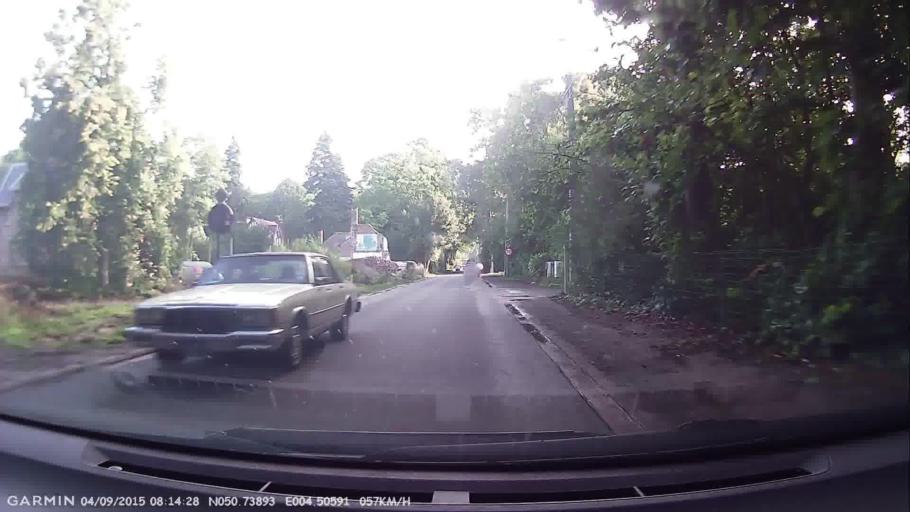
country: BE
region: Wallonia
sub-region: Province du Brabant Wallon
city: La Hulpe
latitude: 50.7392
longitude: 4.5064
